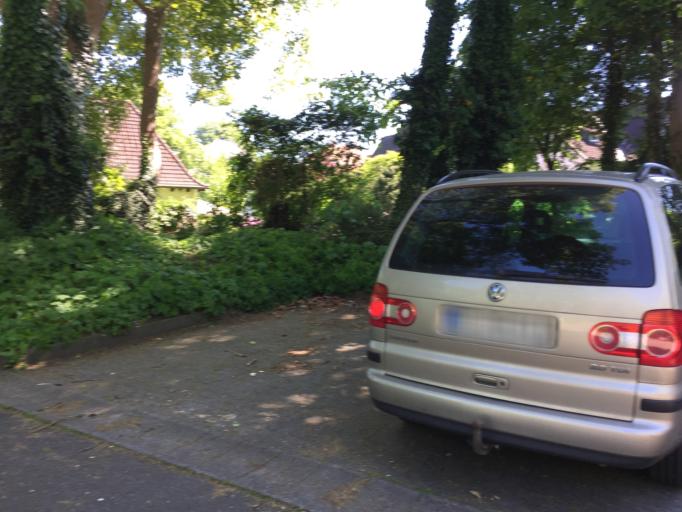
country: DE
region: Schleswig-Holstein
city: Kiel
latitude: 54.3436
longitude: 10.1469
